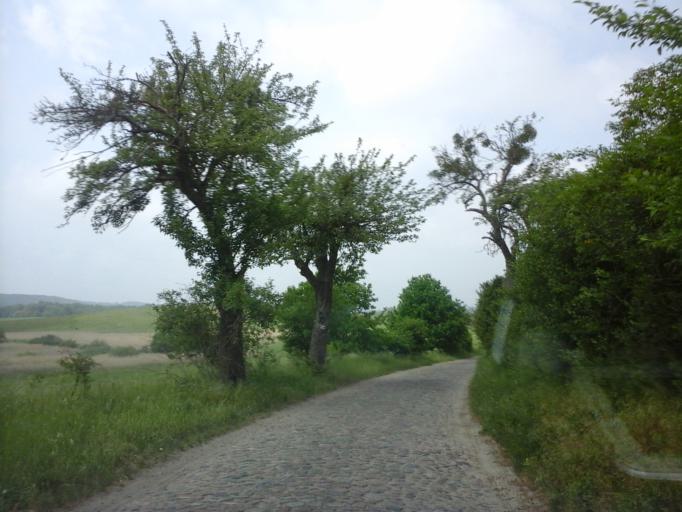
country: PL
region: West Pomeranian Voivodeship
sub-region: Powiat mysliborski
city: Barlinek
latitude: 53.0374
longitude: 15.2158
